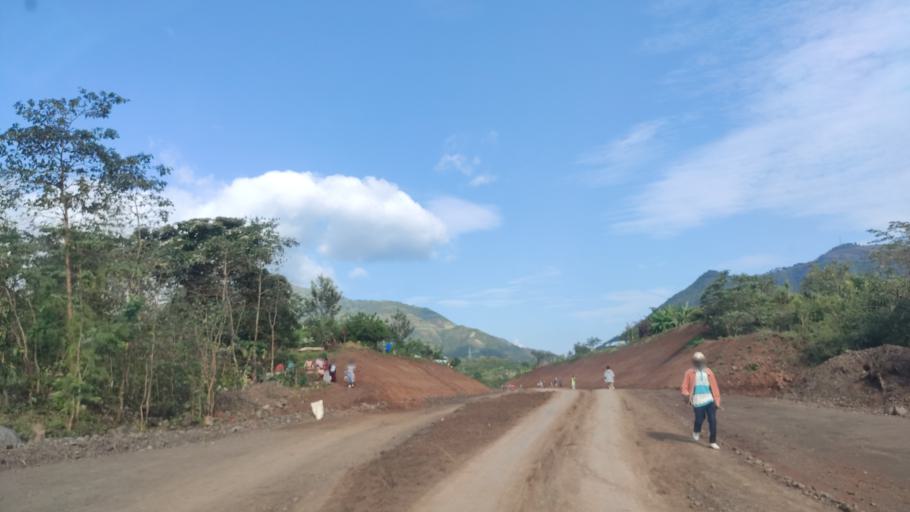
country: ET
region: Southern Nations, Nationalities, and People's Region
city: Felege Neway
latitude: 6.4264
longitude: 37.3205
